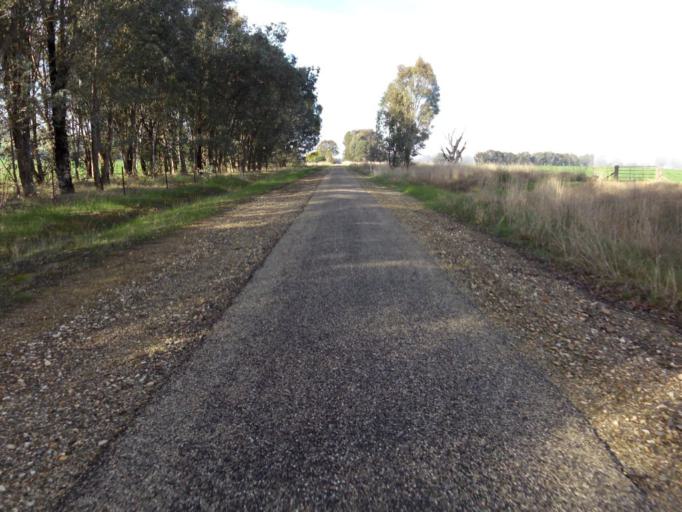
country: AU
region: Victoria
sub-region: Wangaratta
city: Wangaratta
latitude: -36.4326
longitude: 146.5507
